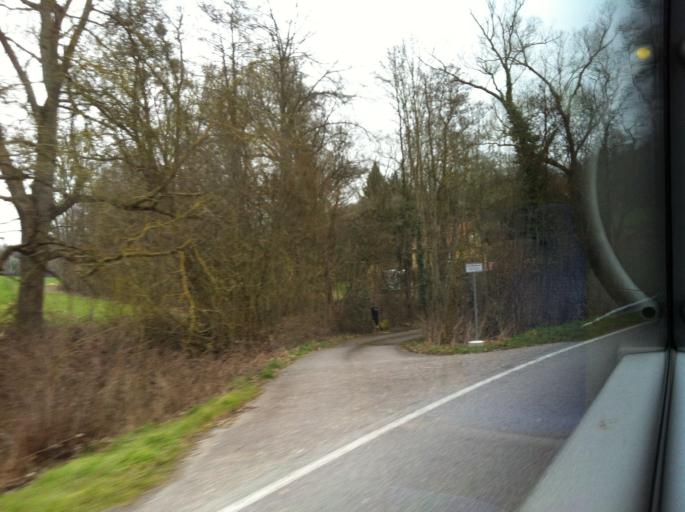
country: DE
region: Baden-Wuerttemberg
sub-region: Karlsruhe Region
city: Fahrenbach
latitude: 49.4045
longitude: 9.1421
